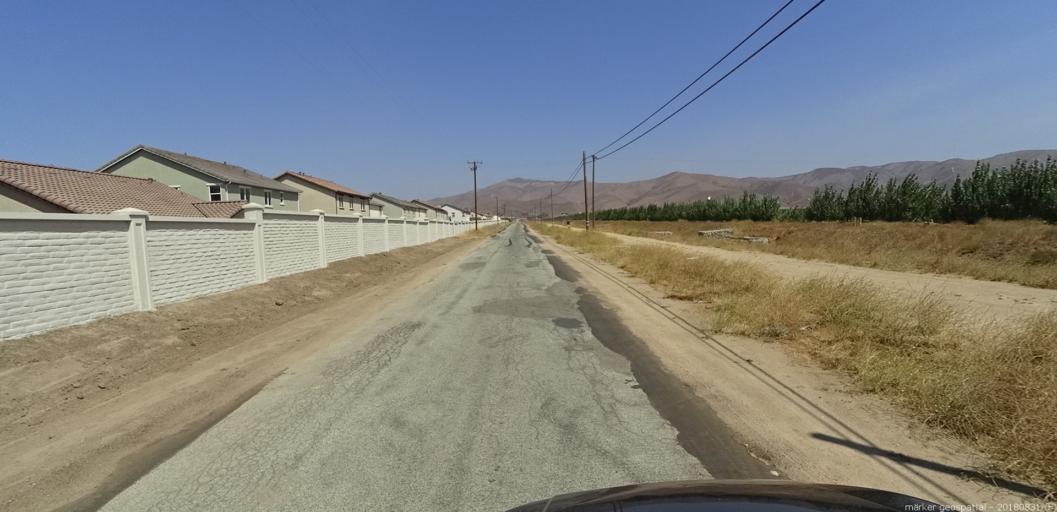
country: US
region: California
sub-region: Monterey County
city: Soledad
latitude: 36.4312
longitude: -121.3113
